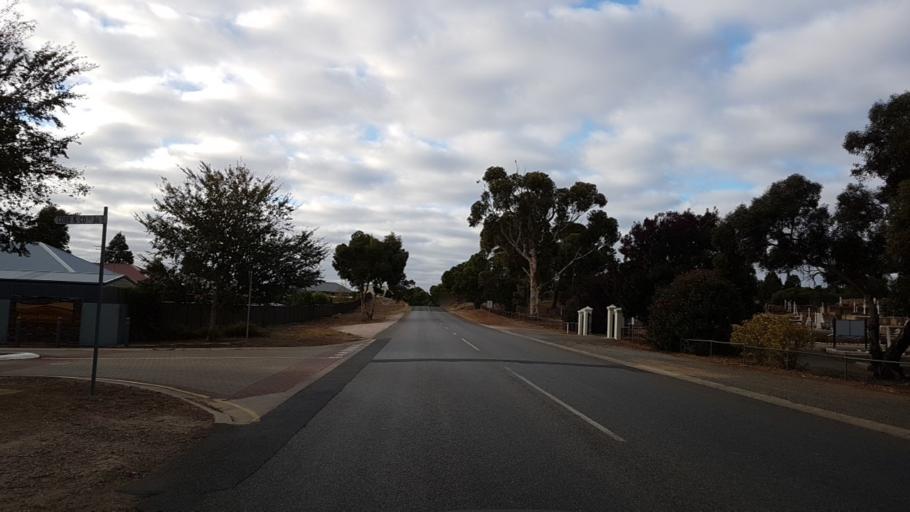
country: AU
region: South Australia
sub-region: Alexandrina
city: Strathalbyn
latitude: -35.2650
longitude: 138.9029
